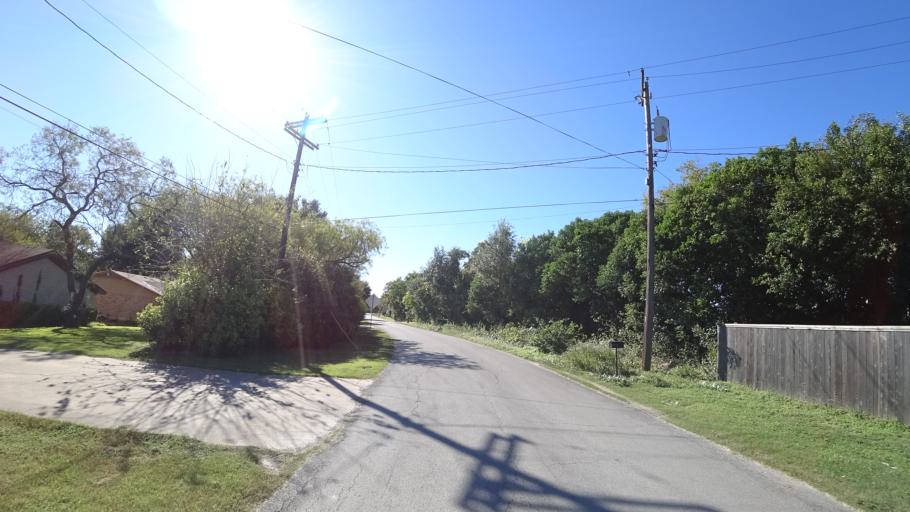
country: US
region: Texas
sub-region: Travis County
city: Manor
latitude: 30.3322
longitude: -97.6556
